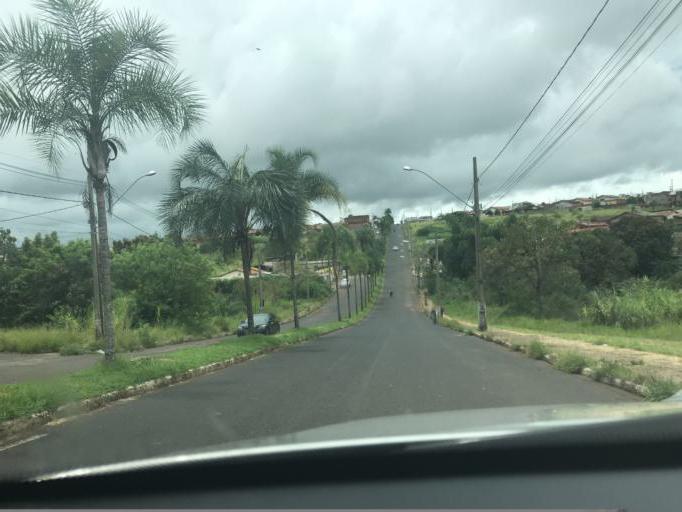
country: BR
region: Minas Gerais
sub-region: Araxa
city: Araxa
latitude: -19.5782
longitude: -46.9326
